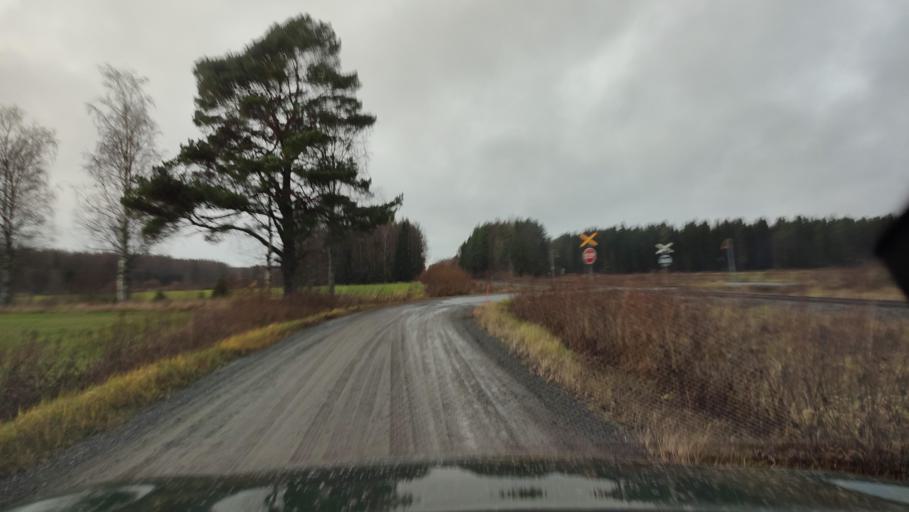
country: FI
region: Ostrobothnia
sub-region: Sydosterbotten
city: Naerpes
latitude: 62.4572
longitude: 21.5031
